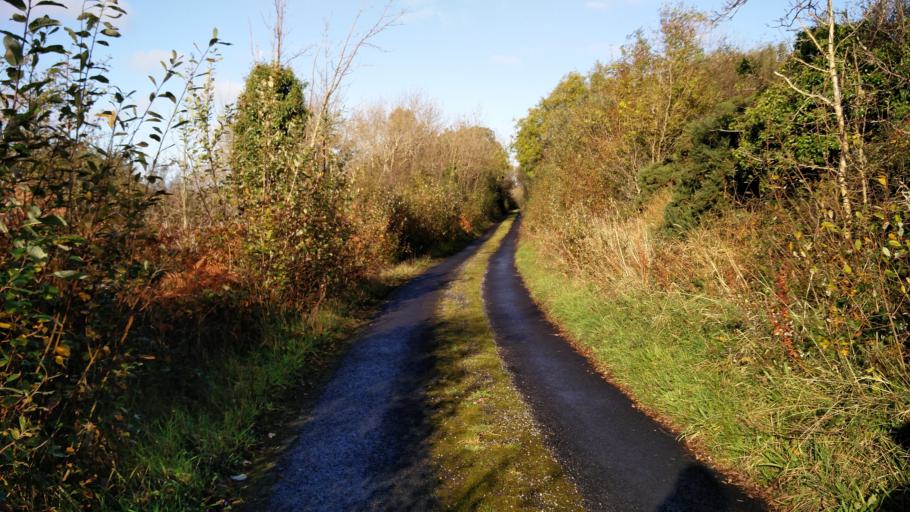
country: IE
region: Connaught
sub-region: Maigh Eo
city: Westport
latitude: 53.7806
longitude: -9.4543
